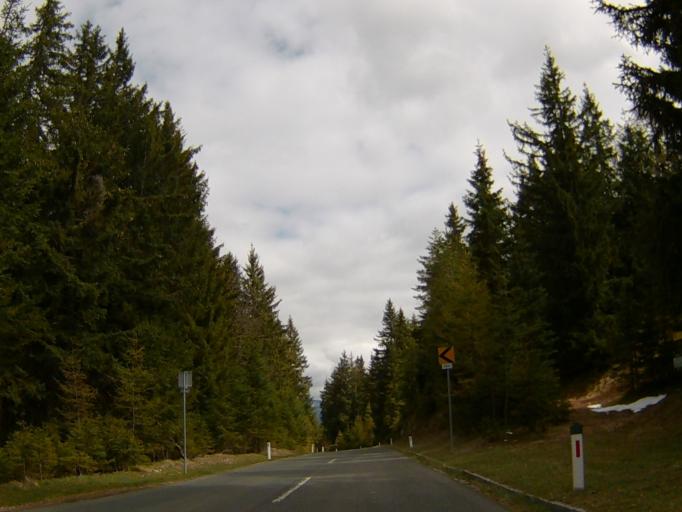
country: AT
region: Carinthia
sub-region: Politischer Bezirk Villach Land
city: Arnoldstein
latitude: 46.5907
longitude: 13.7431
